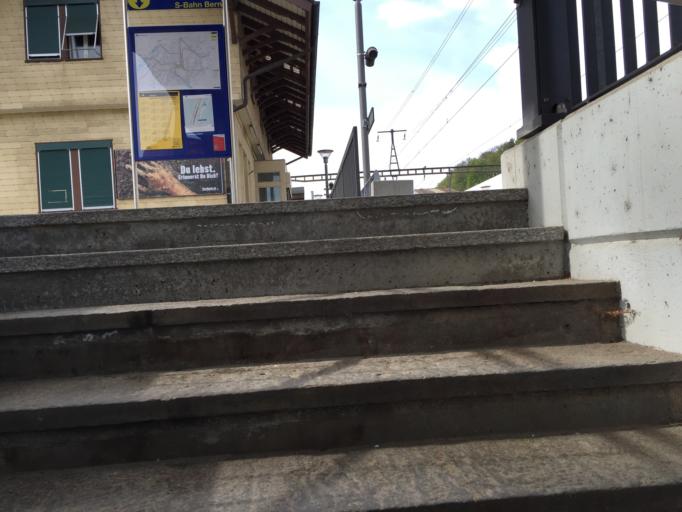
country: CH
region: Fribourg
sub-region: Sense District
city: Flamatt
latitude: 46.9048
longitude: 7.3572
